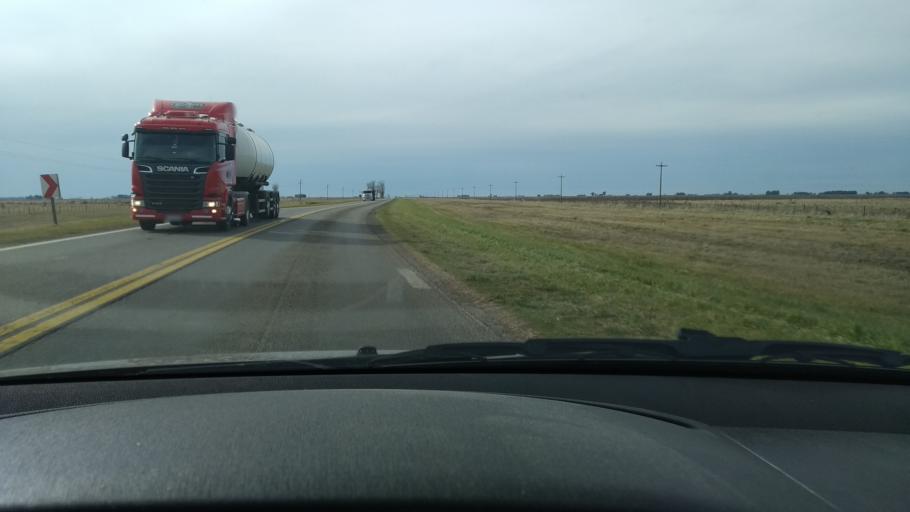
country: AR
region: Buenos Aires
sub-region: Partido de Azul
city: Azul
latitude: -36.7079
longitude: -59.7588
